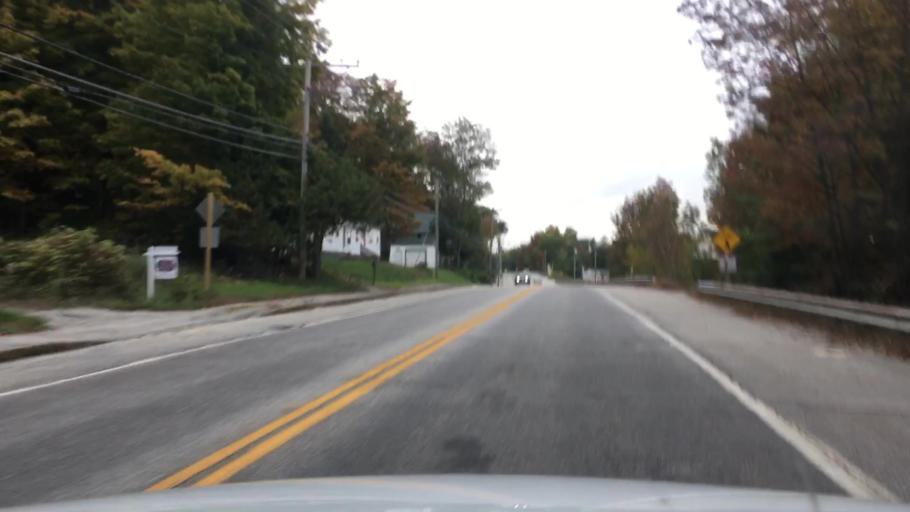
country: US
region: Maine
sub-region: Oxford County
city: Norway
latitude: 44.2134
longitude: -70.5493
